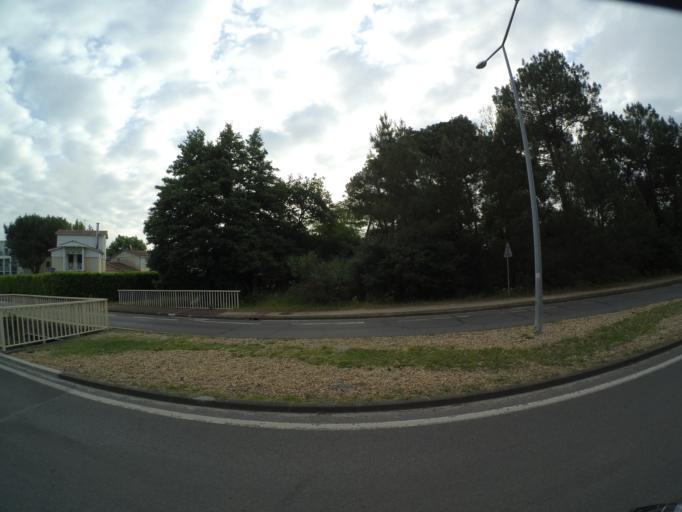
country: FR
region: Aquitaine
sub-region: Departement de la Gironde
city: Pessac
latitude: 44.7987
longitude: -0.6846
